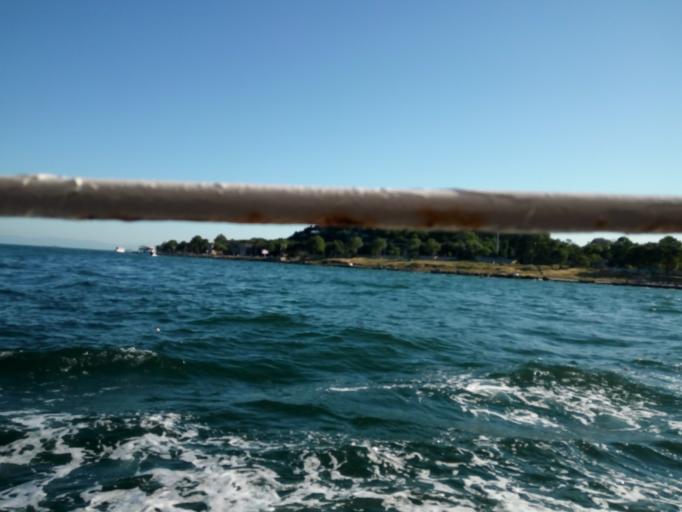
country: TR
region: Istanbul
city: Eminoenue
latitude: 41.0185
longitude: 28.9887
